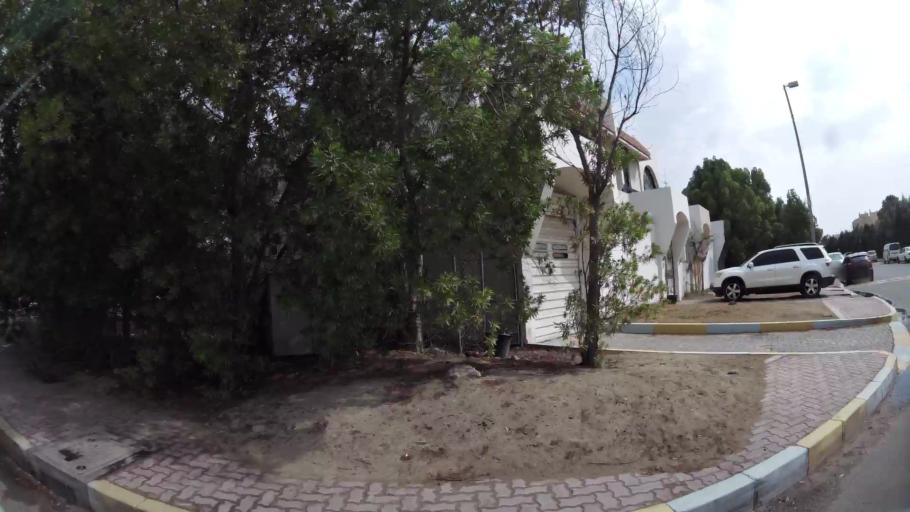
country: AE
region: Abu Dhabi
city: Abu Dhabi
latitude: 24.4358
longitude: 54.4354
